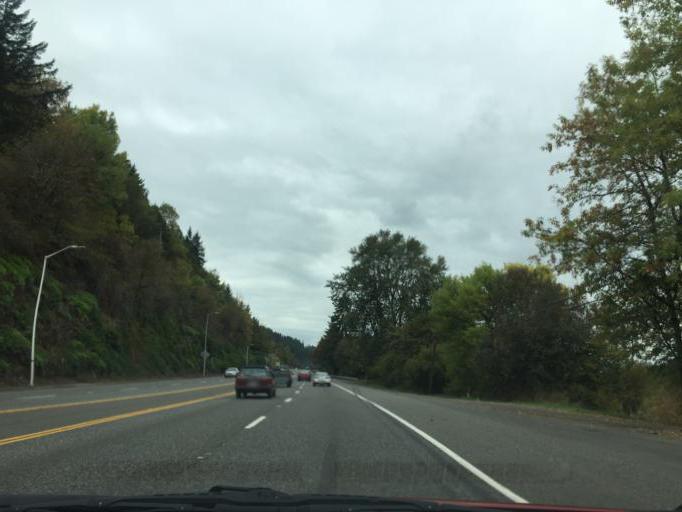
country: US
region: Oregon
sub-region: Washington County
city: Oak Hills
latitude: 45.6129
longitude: -122.7987
